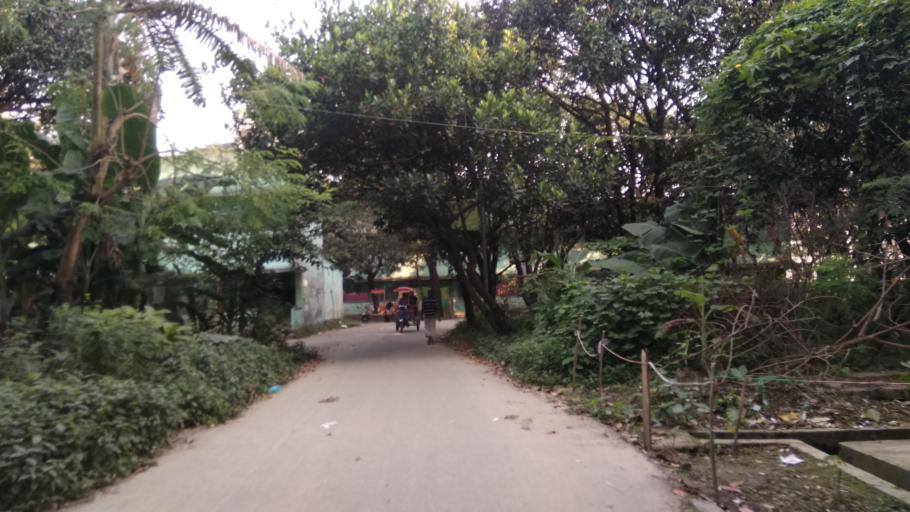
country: BD
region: Dhaka
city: Tungi
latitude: 23.8444
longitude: 90.4181
